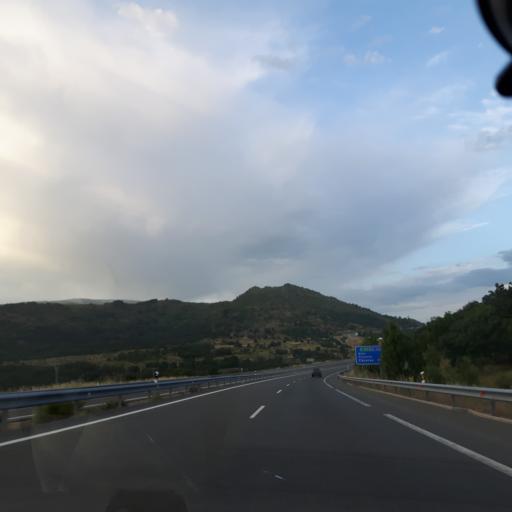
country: ES
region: Castille and Leon
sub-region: Provincia de Salamanca
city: Sorihuela
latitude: 40.4445
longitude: -5.6865
